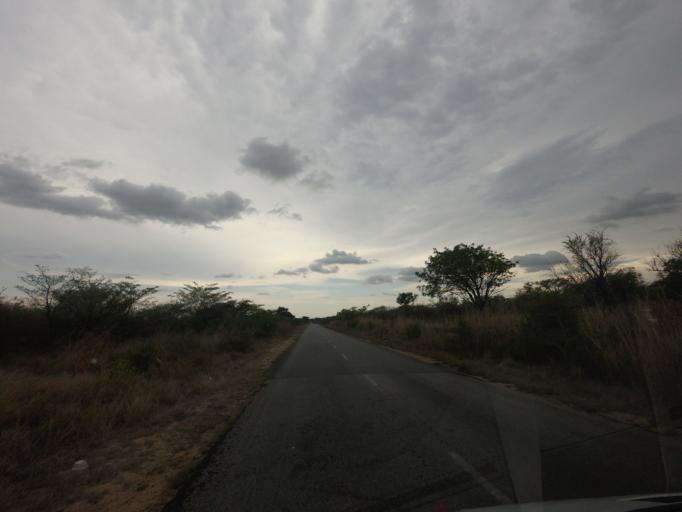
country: ZA
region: Limpopo
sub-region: Mopani District Municipality
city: Hoedspruit
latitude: -24.5285
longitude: 30.9772
